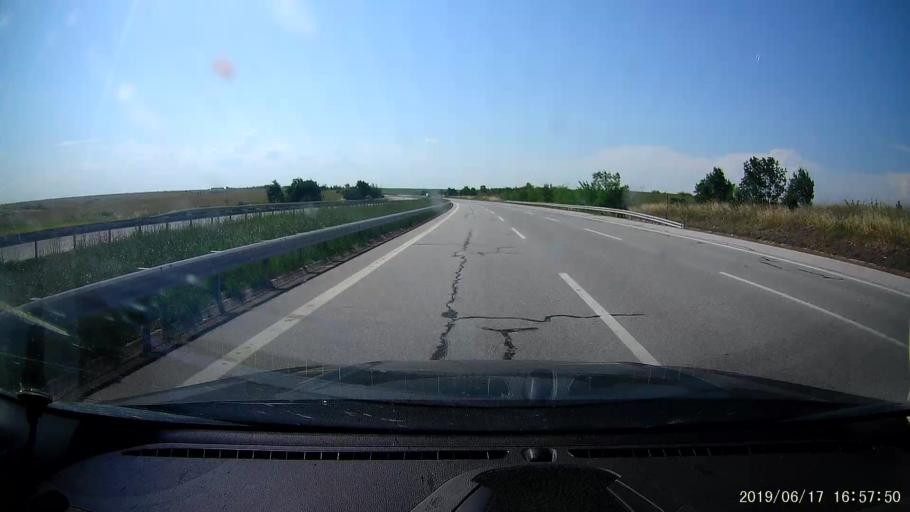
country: TR
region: Edirne
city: Haskoy
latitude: 41.6071
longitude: 26.9053
